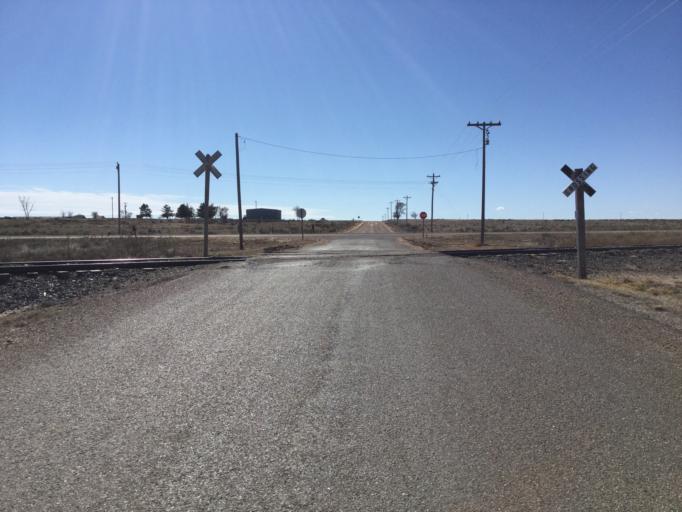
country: US
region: Kansas
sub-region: Morton County
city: Elkhart
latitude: 37.0381
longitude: -101.8452
